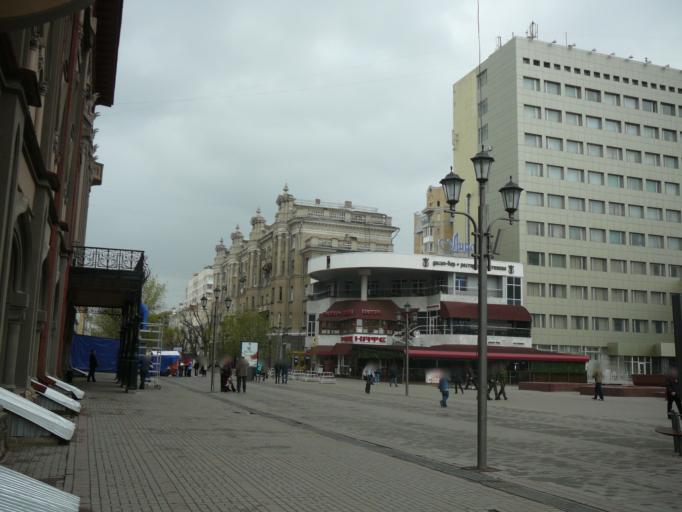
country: RU
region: Saratov
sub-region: Saratovskiy Rayon
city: Saratov
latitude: 51.5299
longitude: 46.0346
